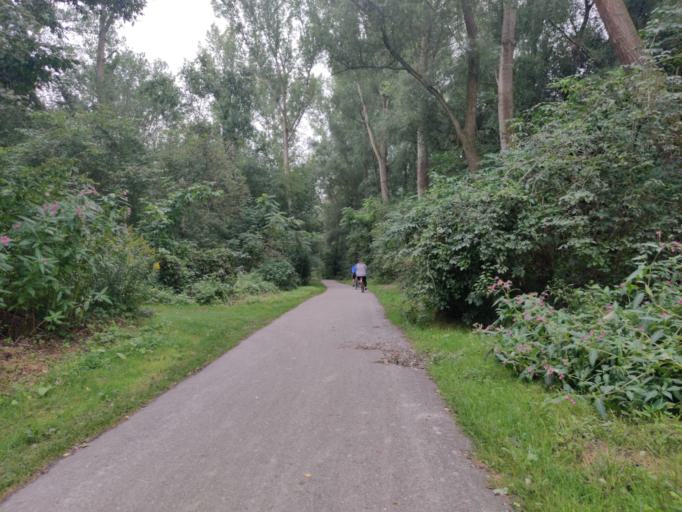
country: AT
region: Lower Austria
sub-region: Politischer Bezirk Tulln
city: Kirchberg am Wagram
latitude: 48.3607
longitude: 15.8797
